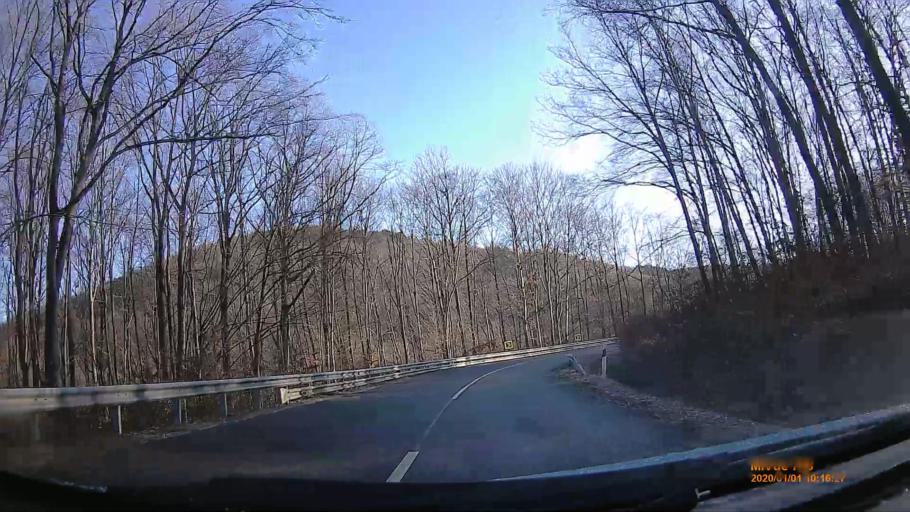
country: HU
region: Heves
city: Paradsasvar
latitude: 47.9138
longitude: 19.9918
